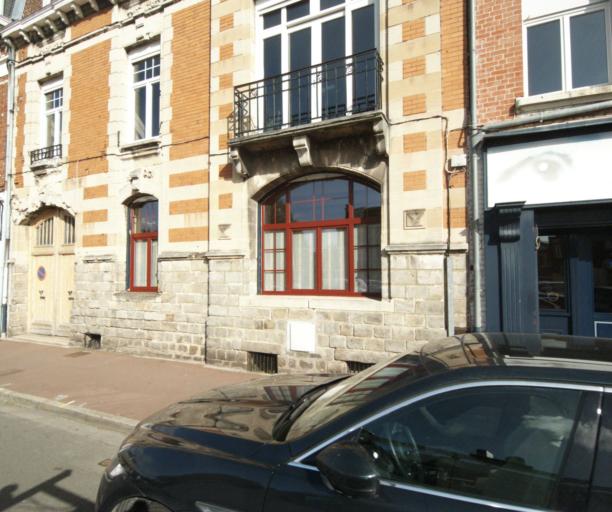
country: FR
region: Nord-Pas-de-Calais
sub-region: Departement du Nord
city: La Bassee
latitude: 50.5317
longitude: 2.8043
